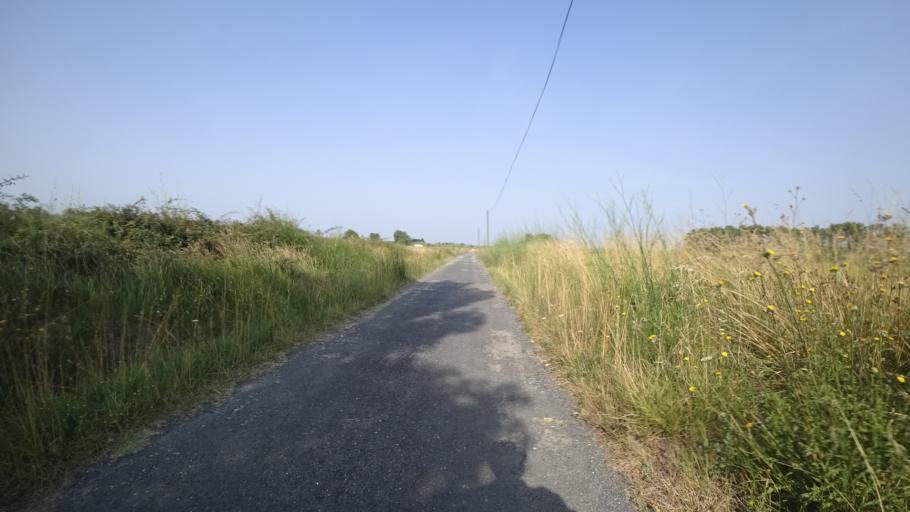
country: FR
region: Languedoc-Roussillon
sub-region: Departement des Pyrenees-Orientales
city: Villelongue-de-la-Salanque
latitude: 42.7346
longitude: 2.9992
